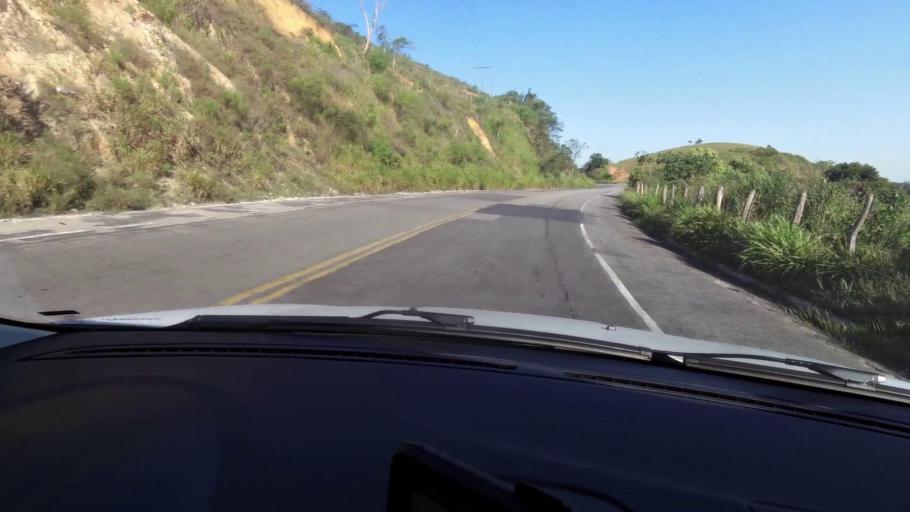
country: BR
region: Espirito Santo
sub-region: Piuma
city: Piuma
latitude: -20.7306
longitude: -40.6526
